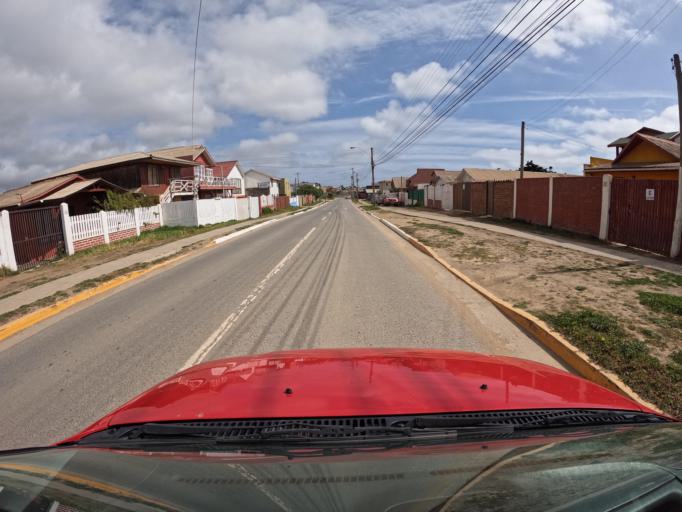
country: CL
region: O'Higgins
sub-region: Provincia de Colchagua
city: Santa Cruz
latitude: -34.3837
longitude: -72.0161
